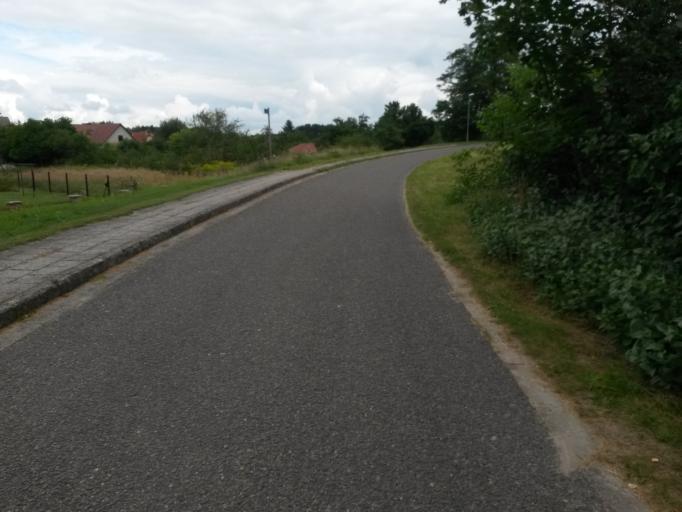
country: PL
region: West Pomeranian Voivodeship
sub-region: Powiat gryfinski
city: Cedynia
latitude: 52.8725
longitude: 14.1463
